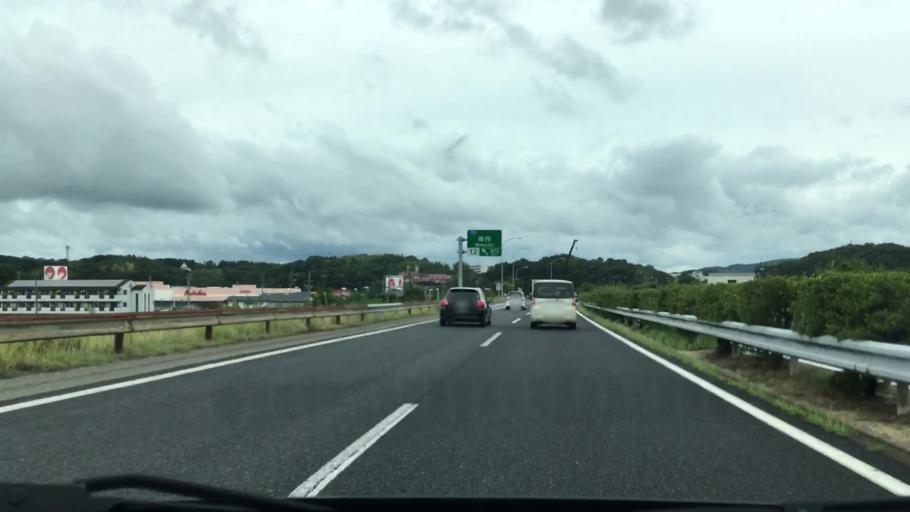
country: JP
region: Okayama
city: Tsuyama
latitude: 35.0247
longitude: 134.1664
